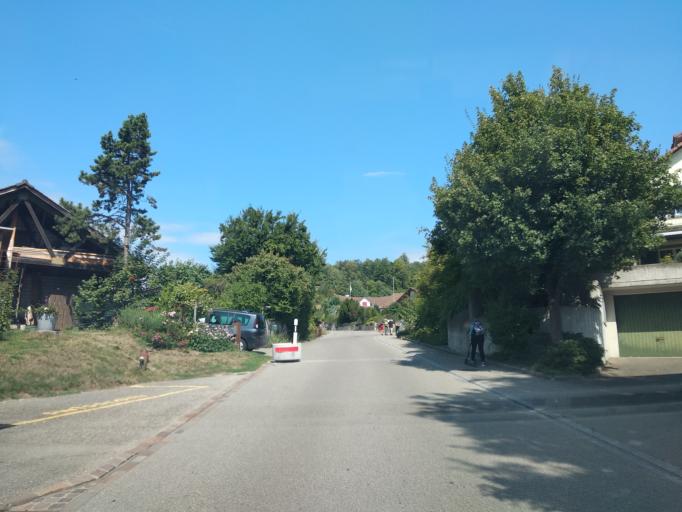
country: CH
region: Thurgau
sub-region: Frauenfeld District
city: Gachnang
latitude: 47.5812
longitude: 8.8309
